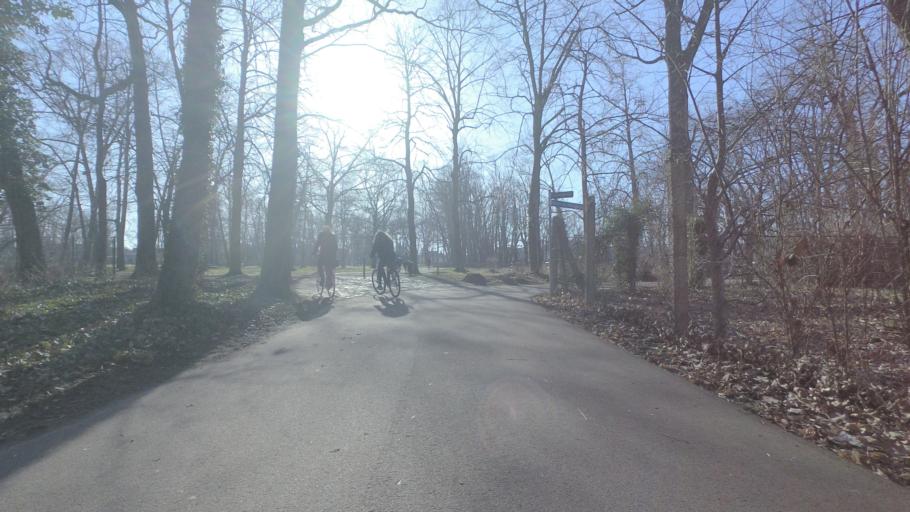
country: DE
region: Brandenburg
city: Luckenwalde
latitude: 52.0825
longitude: 13.1743
